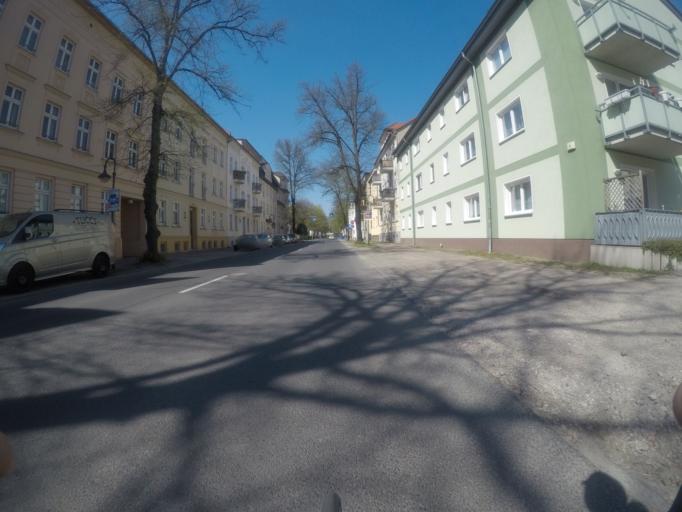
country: DE
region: Brandenburg
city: Bernau bei Berlin
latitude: 52.6796
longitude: 13.5935
